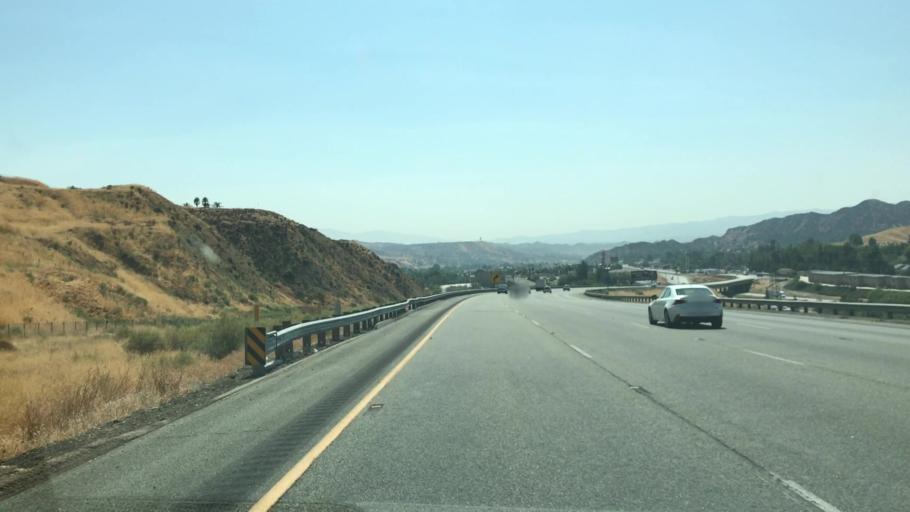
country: US
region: California
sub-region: Los Angeles County
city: Castaic
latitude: 34.5079
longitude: -118.6295
